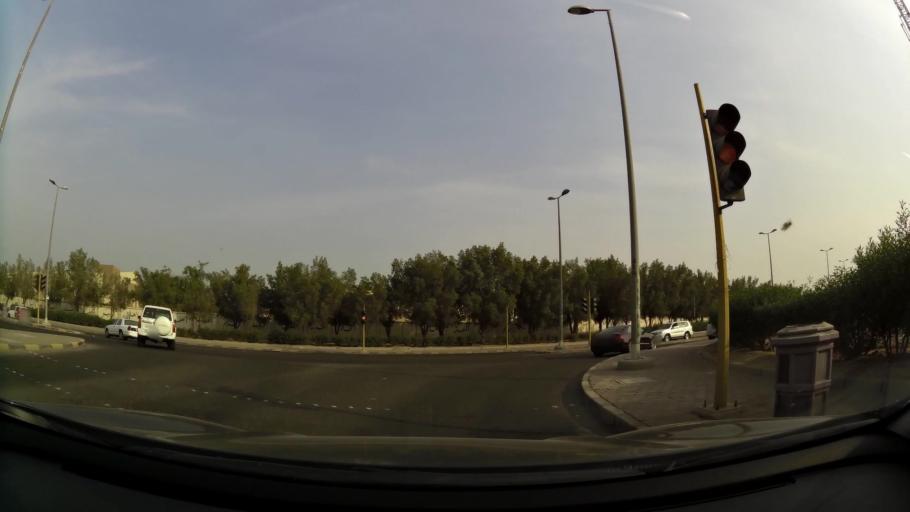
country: KW
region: Mubarak al Kabir
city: Sabah as Salim
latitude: 29.2435
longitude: 48.0608
